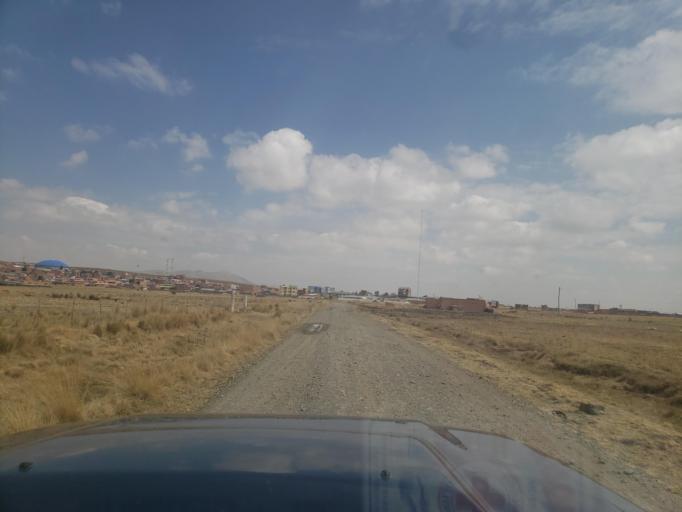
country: BO
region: La Paz
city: Batallas
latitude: -16.4013
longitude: -68.4678
